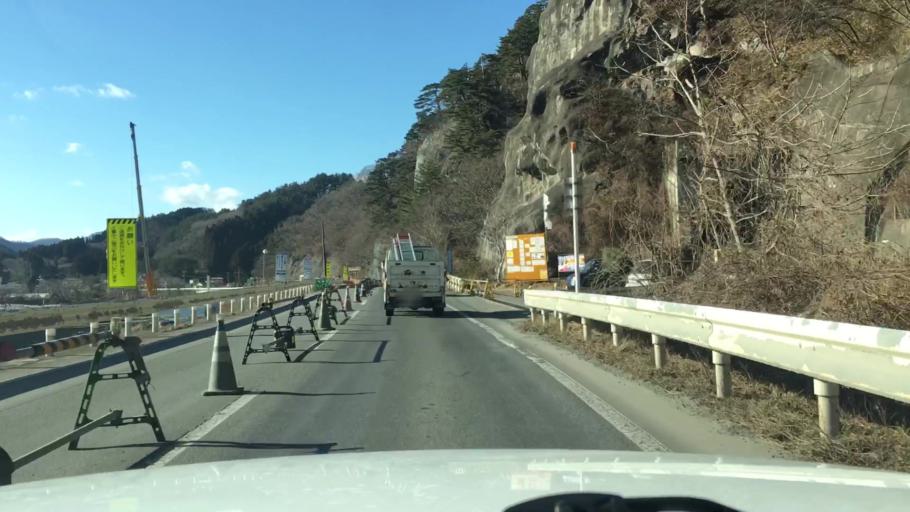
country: JP
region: Iwate
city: Miyako
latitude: 39.6320
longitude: 141.8686
